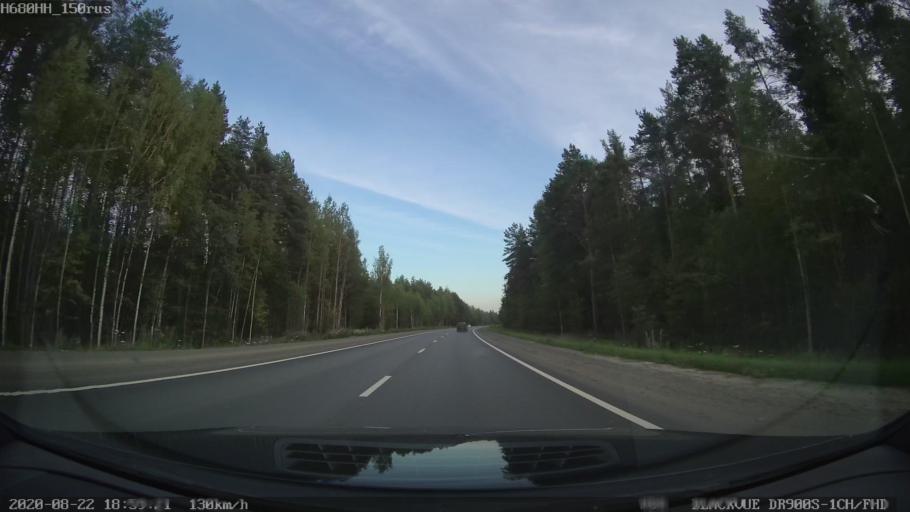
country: RU
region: Tverskaya
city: Rameshki
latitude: 57.1444
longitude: 36.0952
